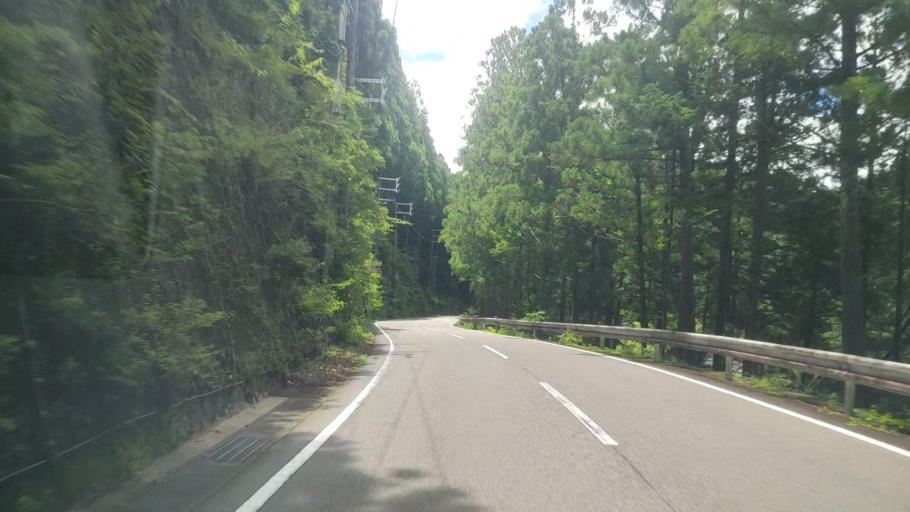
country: JP
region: Mie
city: Owase
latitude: 33.9678
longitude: 136.0614
